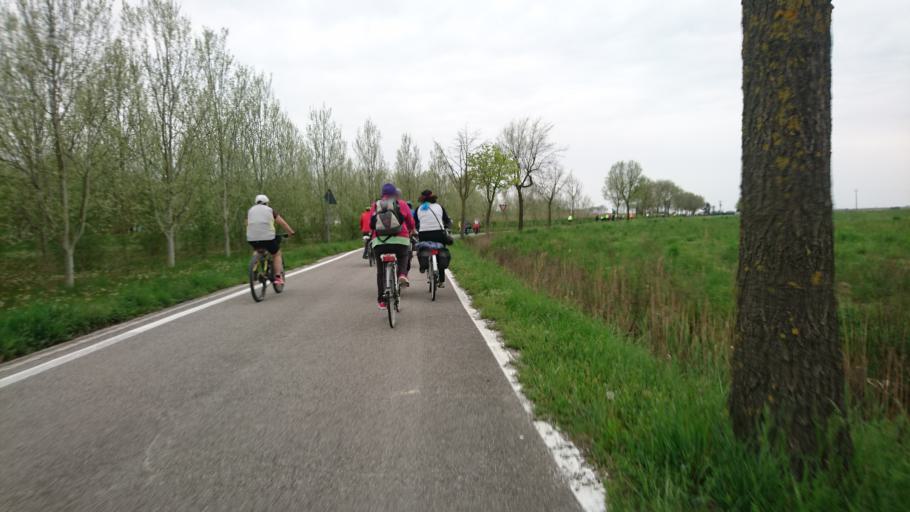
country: IT
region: Veneto
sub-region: Provincia di Venezia
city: Cesarolo
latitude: 45.6852
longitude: 12.9920
